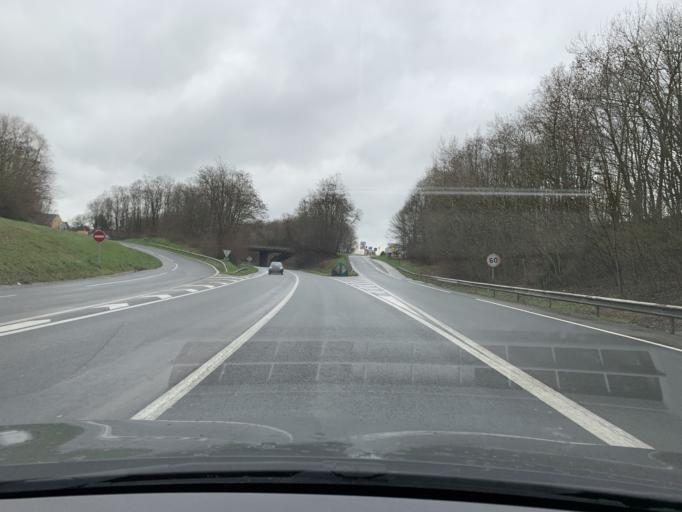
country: FR
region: Nord-Pas-de-Calais
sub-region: Departement du Nord
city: Dechy
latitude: 50.3527
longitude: 3.1219
